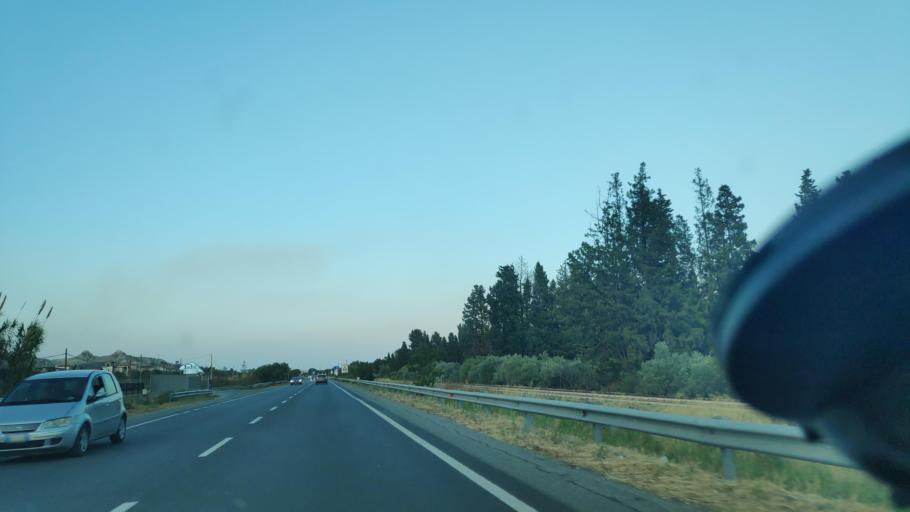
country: IT
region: Calabria
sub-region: Provincia di Reggio Calabria
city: Caulonia Marina
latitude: 38.3312
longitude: 16.4334
